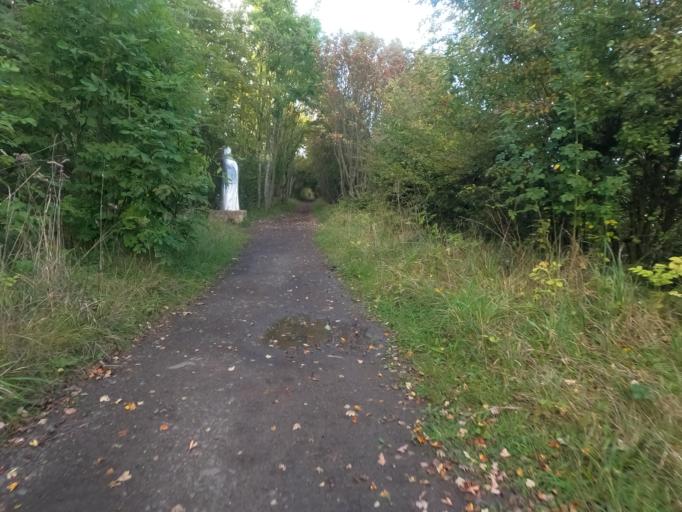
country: GB
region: England
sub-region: Northumberland
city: Seghill
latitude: 55.0733
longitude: -1.5489
